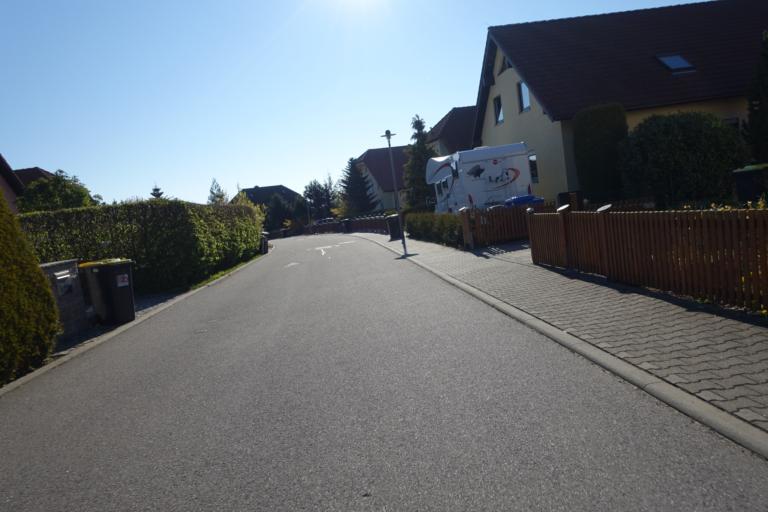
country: DE
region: Saxony
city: Brand-Erbisdorf
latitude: 50.8808
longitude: 13.3423
